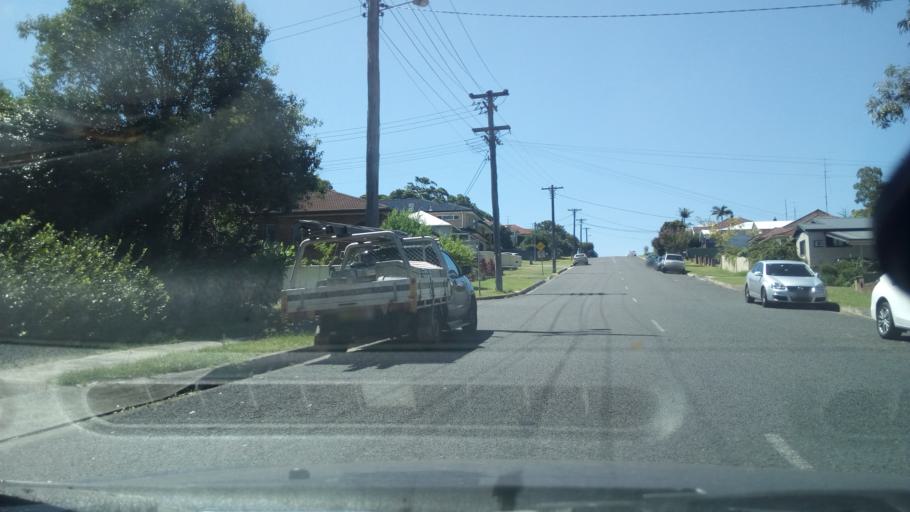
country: AU
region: New South Wales
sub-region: Wollongong
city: Gwynneville
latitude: -34.4243
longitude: 150.8776
